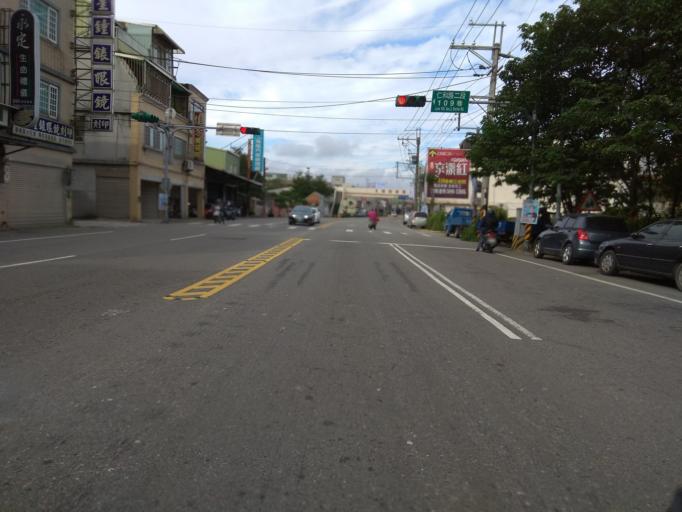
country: TW
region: Taiwan
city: Daxi
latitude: 24.9031
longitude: 121.2677
